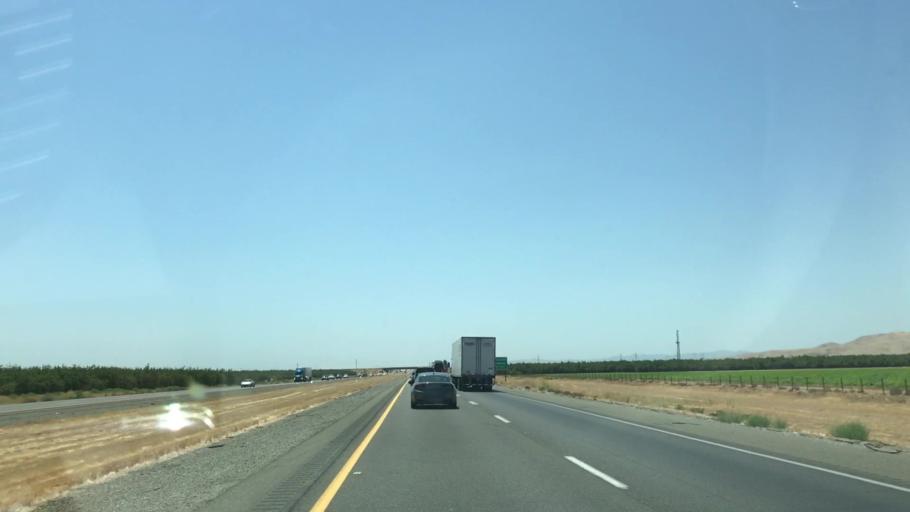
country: US
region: California
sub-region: Merced County
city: South Dos Palos
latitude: 36.7896
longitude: -120.7318
